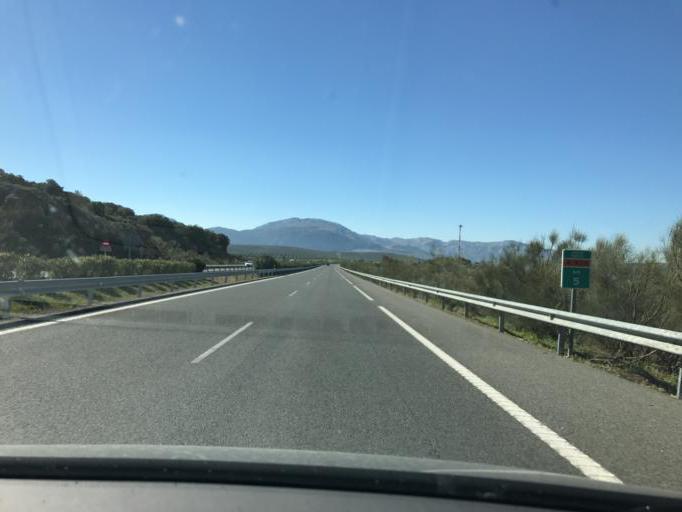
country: ES
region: Andalusia
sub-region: Provincia de Malaga
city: Villanueva del Trabuco
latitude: 37.0941
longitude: -4.3157
